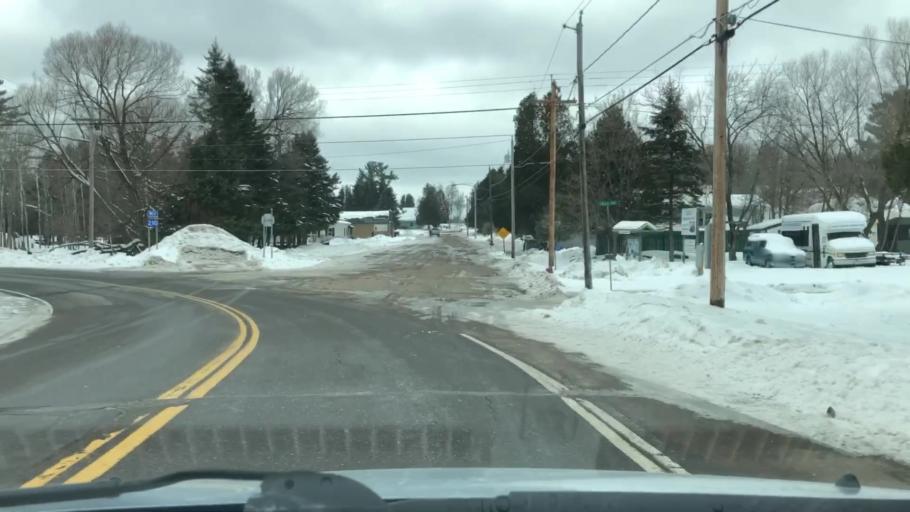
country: US
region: Minnesota
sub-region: Carlton County
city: Carlton
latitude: 46.6640
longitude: -92.3991
